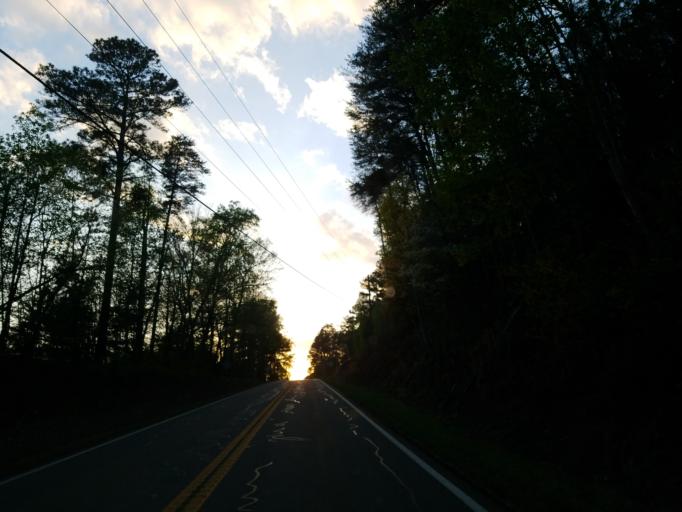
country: US
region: Georgia
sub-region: Pickens County
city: Jasper
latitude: 34.5119
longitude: -84.4446
